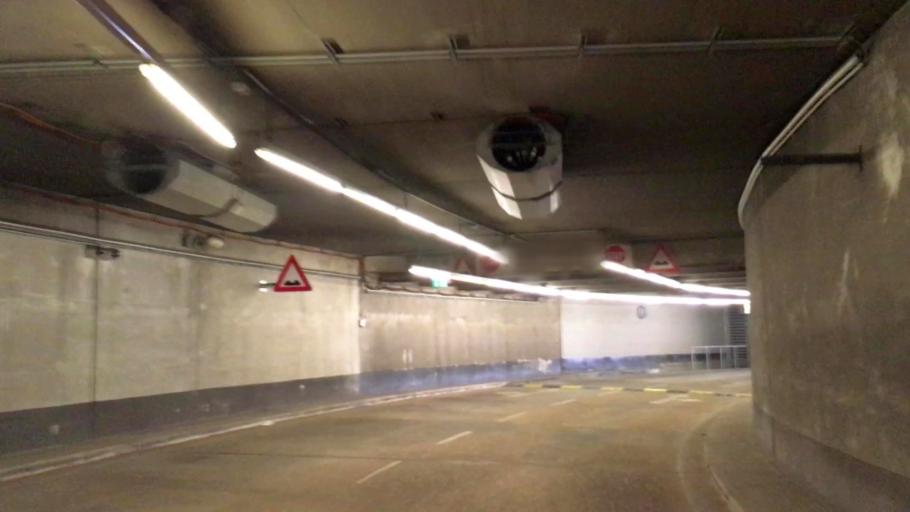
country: AT
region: Vienna
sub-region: Wien Stadt
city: Vienna
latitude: 48.2185
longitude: 16.3444
